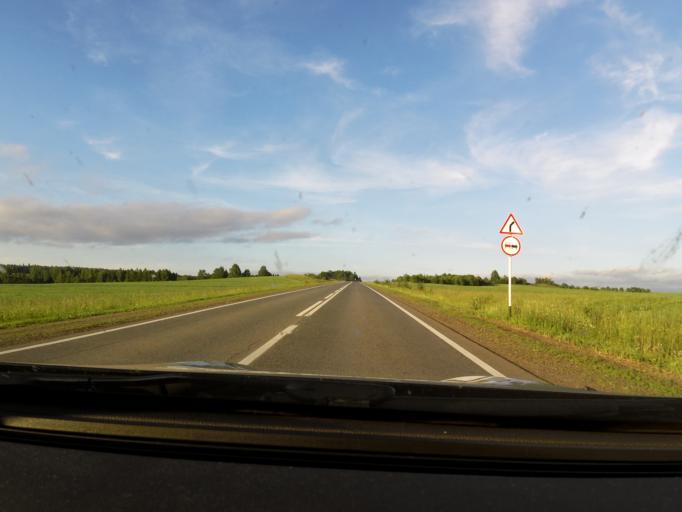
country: RU
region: Perm
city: Siva
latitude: 58.4886
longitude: 54.1045
